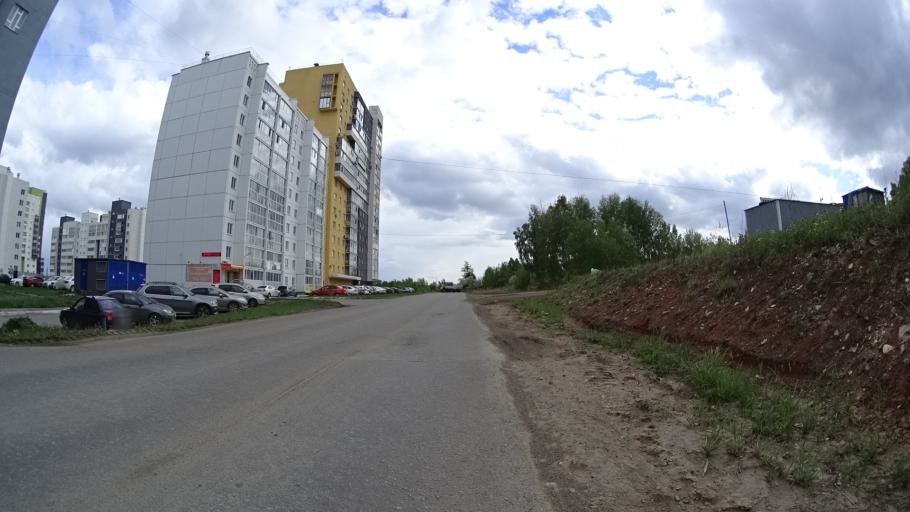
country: RU
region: Chelyabinsk
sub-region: Gorod Chelyabinsk
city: Chelyabinsk
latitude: 55.1611
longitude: 61.2857
